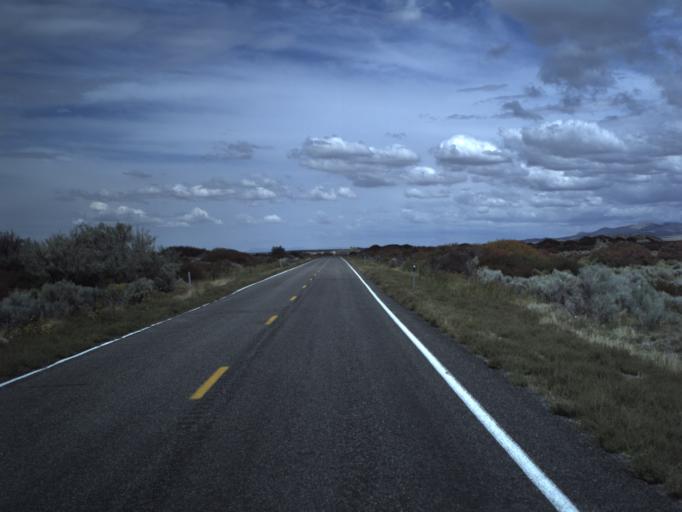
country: US
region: Utah
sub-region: Millard County
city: Fillmore
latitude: 39.1217
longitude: -112.4094
